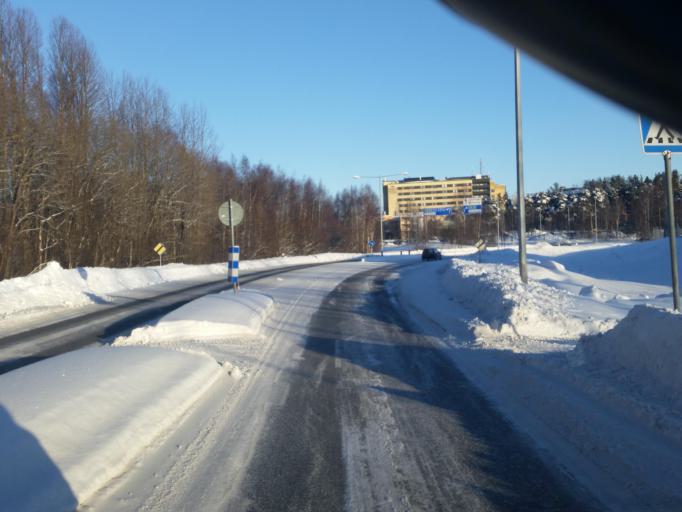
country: SE
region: Norrbotten
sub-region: Pitea Kommun
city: Pitea
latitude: 65.3087
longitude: 21.4942
